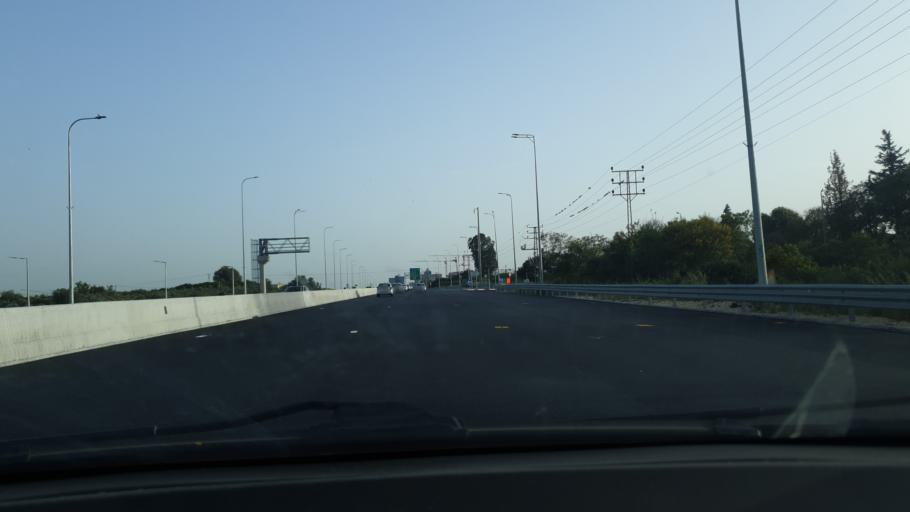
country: IL
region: Central District
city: Ra'anana
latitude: 32.2111
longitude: 34.8837
